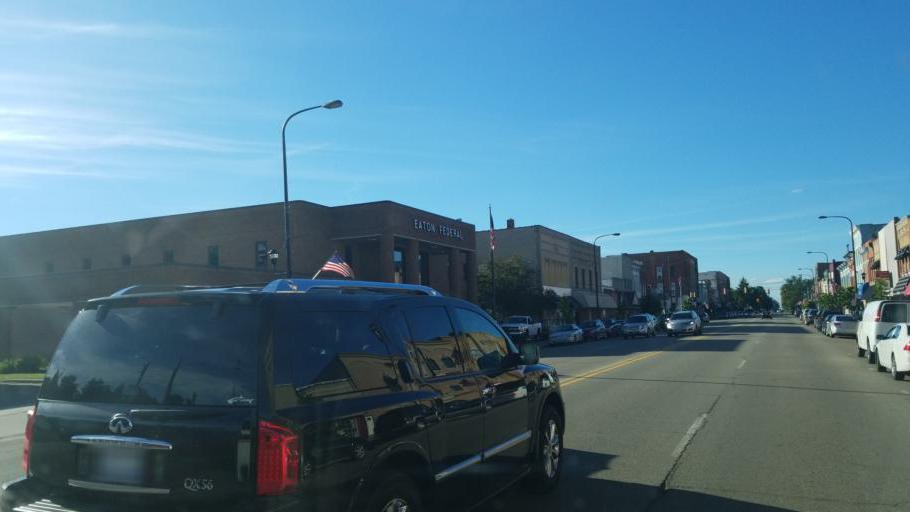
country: US
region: Michigan
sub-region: Eaton County
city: Charlotte
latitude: 42.5609
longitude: -84.8358
